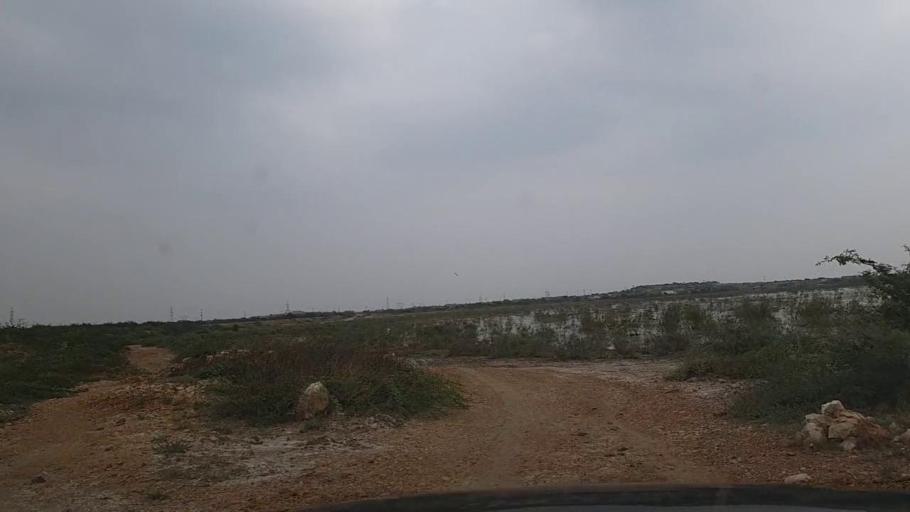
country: PK
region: Sindh
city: Thatta
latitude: 24.8176
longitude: 67.8282
